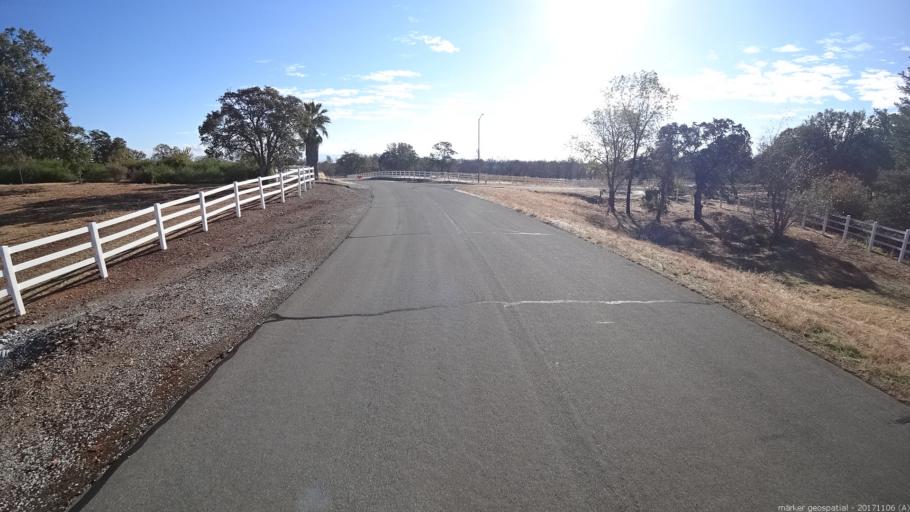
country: US
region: California
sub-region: Shasta County
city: Palo Cedro
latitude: 40.5030
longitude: -122.2448
